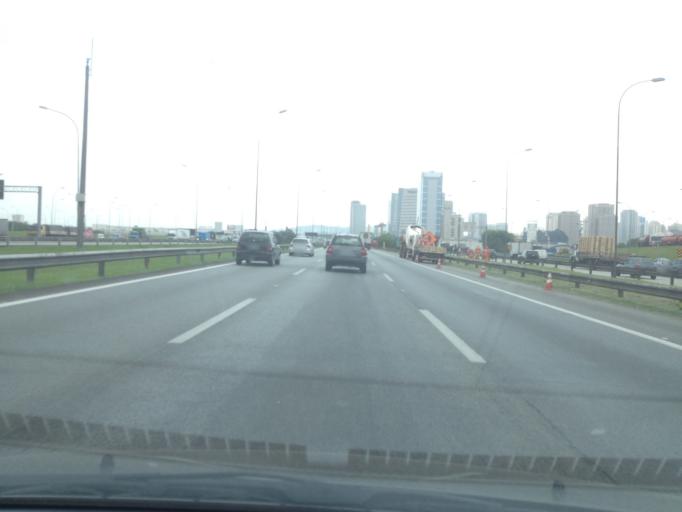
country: BR
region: Sao Paulo
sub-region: Carapicuiba
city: Carapicuiba
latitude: -23.5078
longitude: -46.8286
